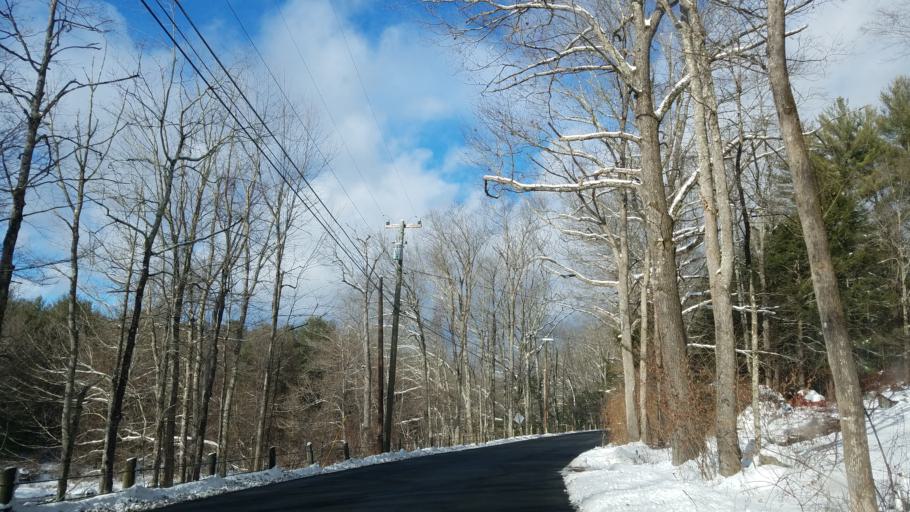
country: US
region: Connecticut
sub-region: Litchfield County
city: Winsted
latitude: 41.9626
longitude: -73.0226
